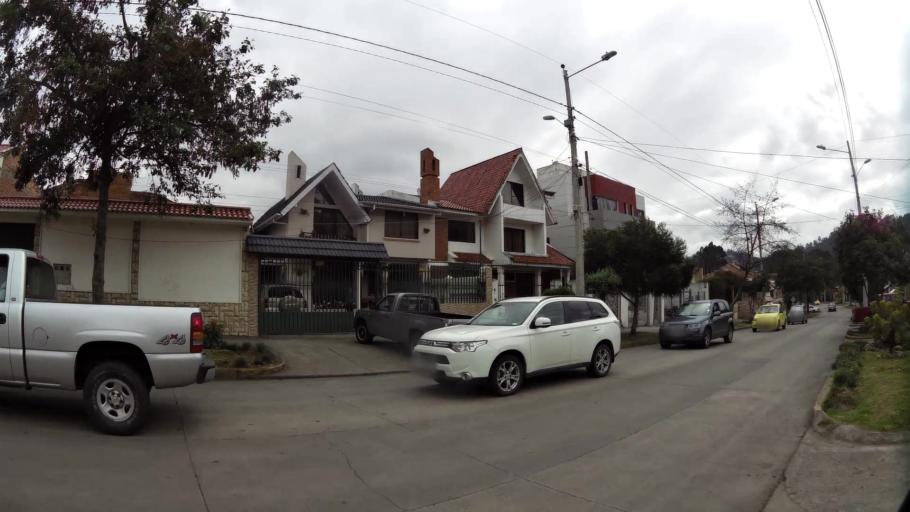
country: EC
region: Azuay
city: Cuenca
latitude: -2.9160
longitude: -79.0008
